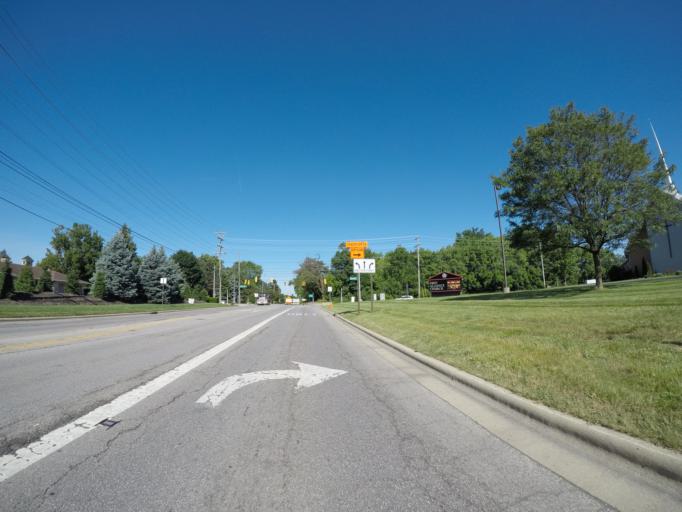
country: US
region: Ohio
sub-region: Franklin County
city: Dublin
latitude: 40.0608
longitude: -83.0926
